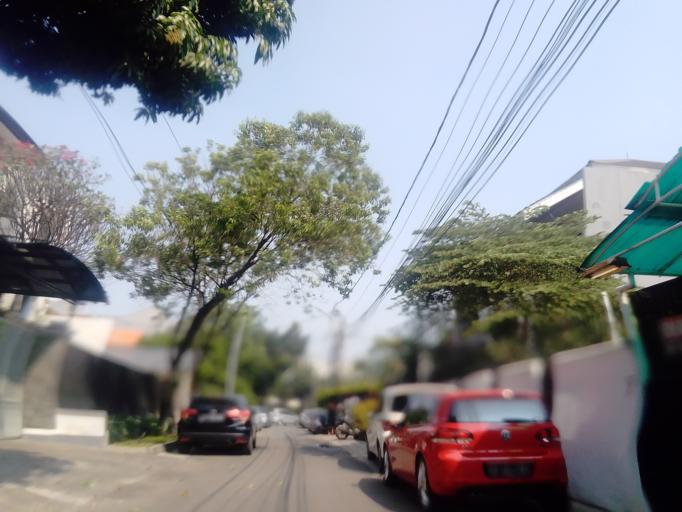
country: ID
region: Jakarta Raya
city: Jakarta
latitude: -6.2509
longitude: 106.7989
